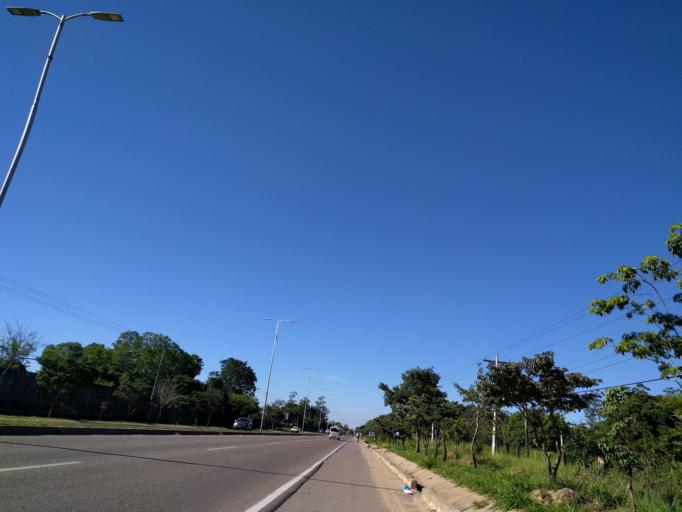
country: BO
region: Santa Cruz
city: Santa Rita
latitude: -17.8723
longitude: -63.2765
